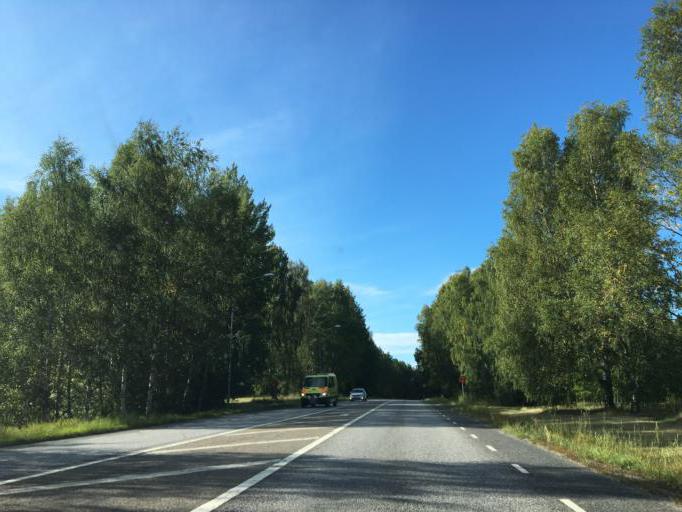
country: SE
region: Soedermanland
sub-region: Nykopings Kommun
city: Nykoping
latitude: 58.7774
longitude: 16.9741
